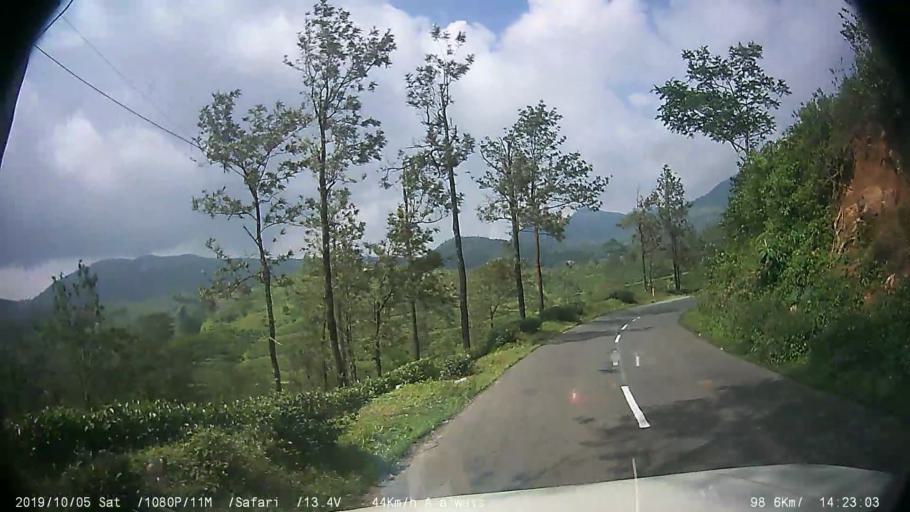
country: IN
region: Kerala
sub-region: Kottayam
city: Erattupetta
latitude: 9.5889
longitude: 76.9665
